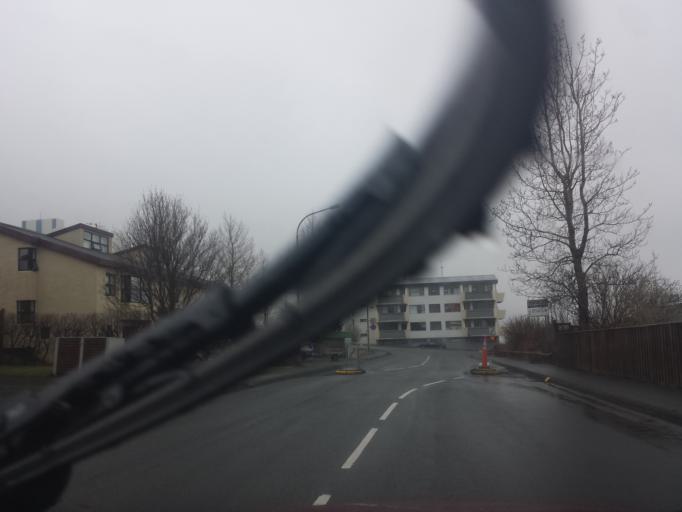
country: IS
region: Capital Region
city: Reykjavik
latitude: 64.1140
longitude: -21.8655
